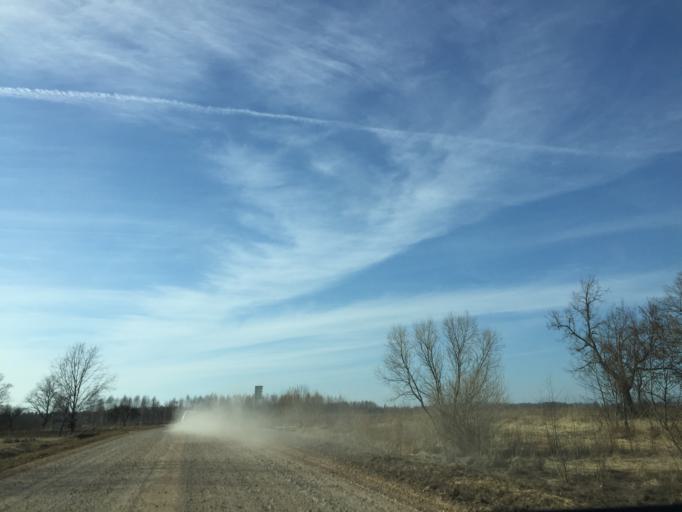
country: LV
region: Saulkrastu
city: Saulkrasti
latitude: 57.2865
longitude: 24.4882
